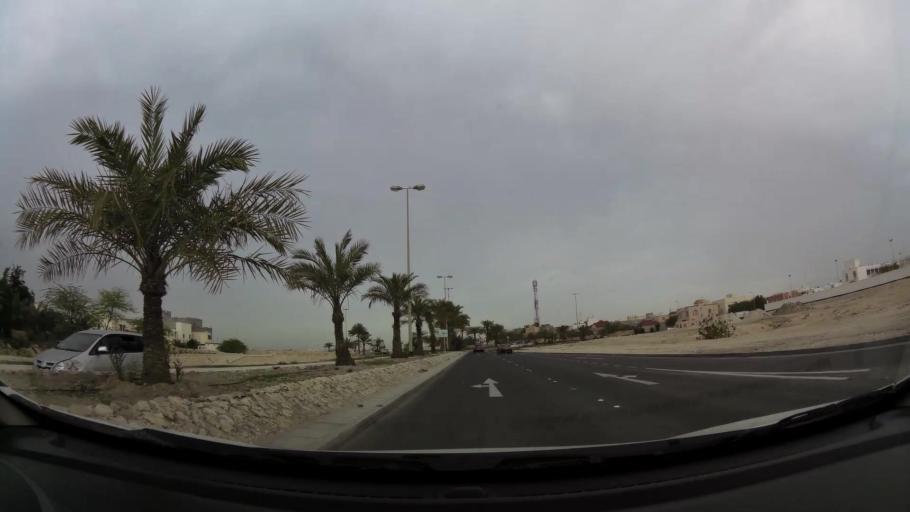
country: BH
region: Central Governorate
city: Dar Kulayb
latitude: 26.0705
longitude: 50.5077
